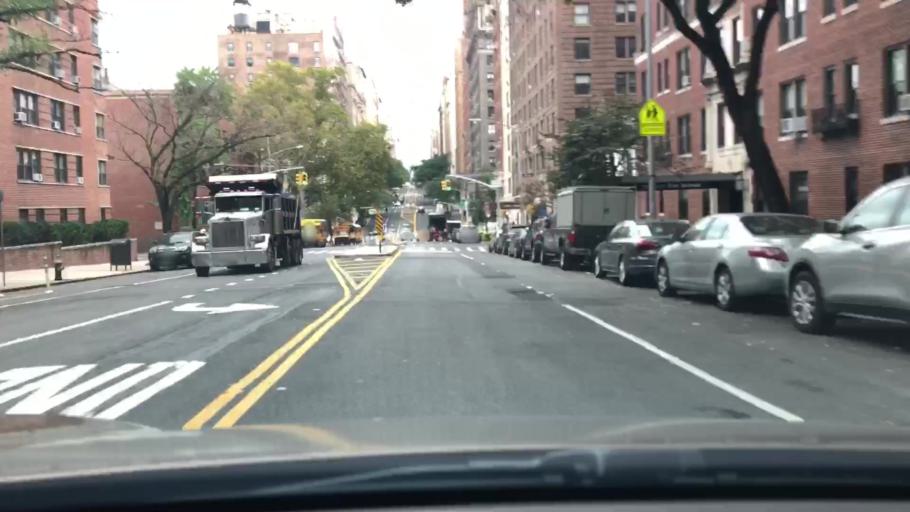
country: US
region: New York
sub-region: New York County
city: Manhattan
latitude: 40.7941
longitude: -73.9741
